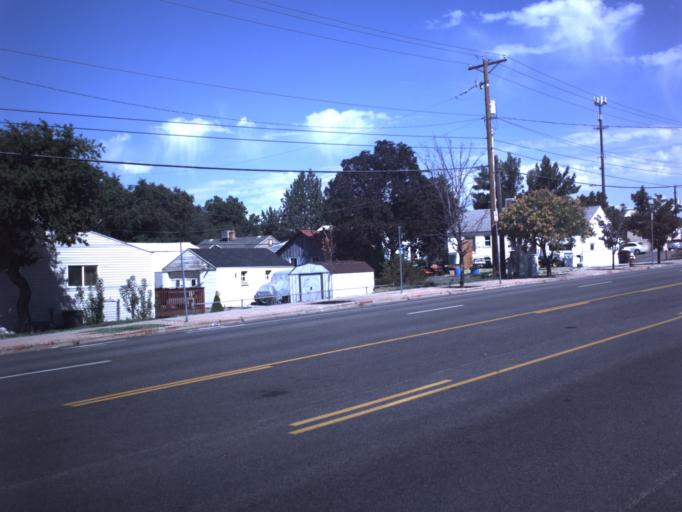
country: US
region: Utah
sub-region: Davis County
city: Clearfield
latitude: 41.1203
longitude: -112.0260
